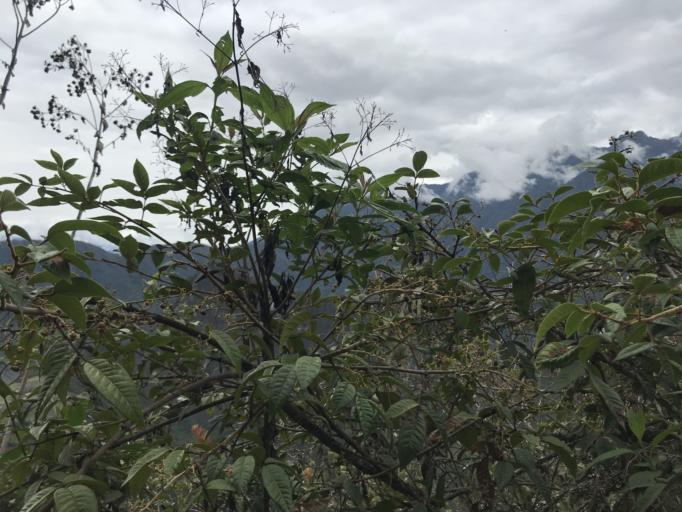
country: PE
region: Cusco
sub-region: Provincia de La Convencion
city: Santa Teresa
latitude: -13.1697
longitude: -72.5349
